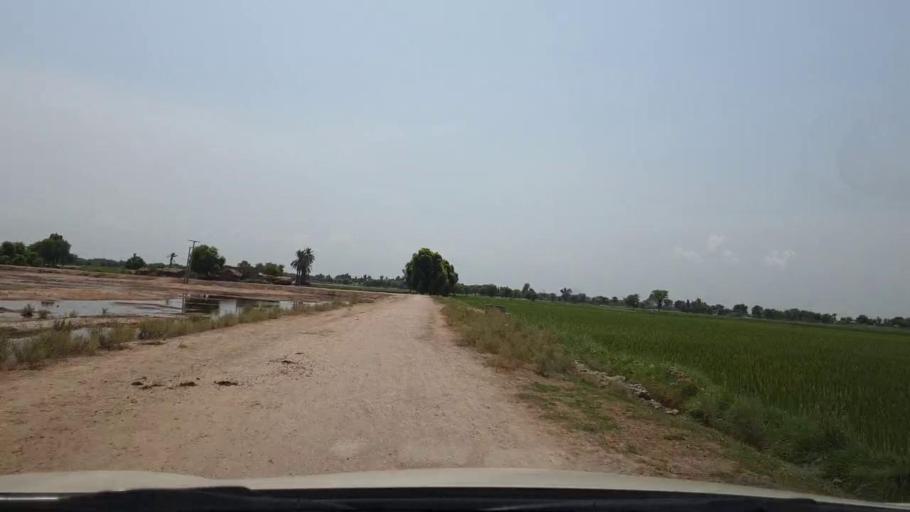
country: PK
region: Sindh
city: Ratodero
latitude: 27.8102
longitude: 68.2428
